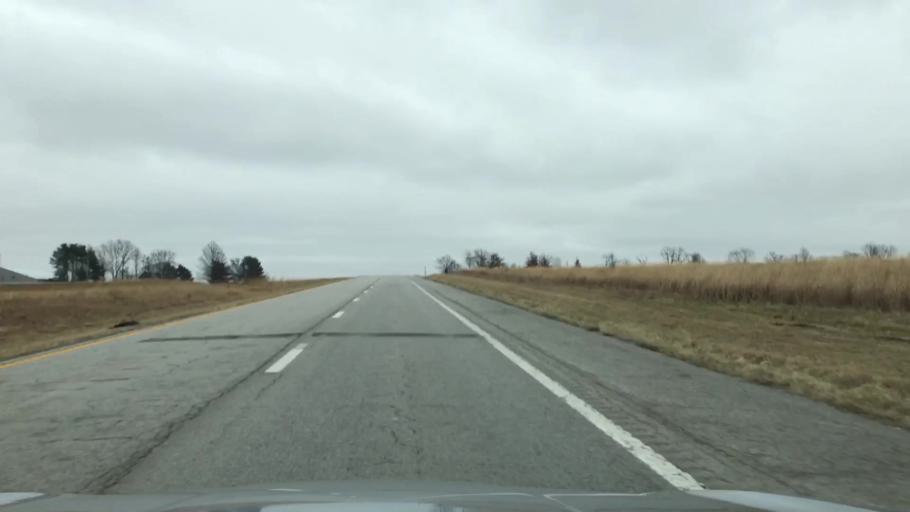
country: US
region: Missouri
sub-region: Linn County
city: Brookfield
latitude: 39.7785
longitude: -93.1598
